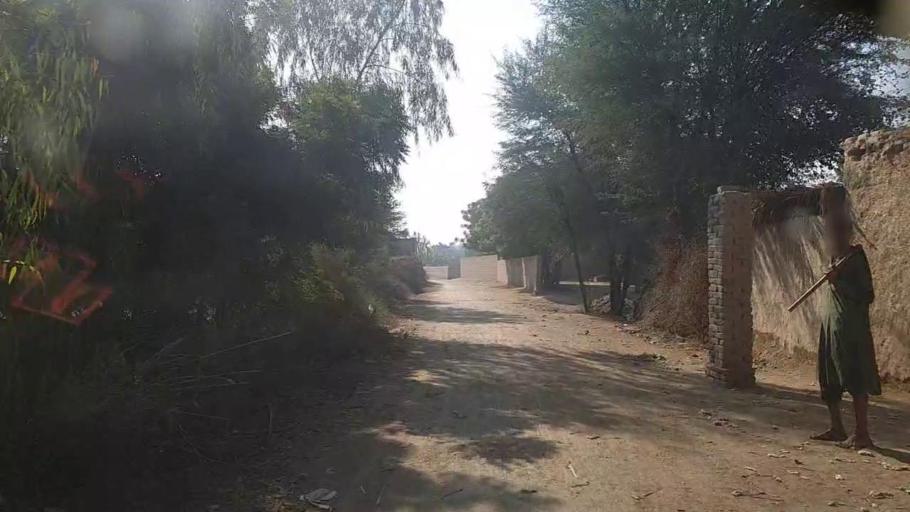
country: PK
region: Sindh
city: Kandiari
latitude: 27.0226
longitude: 68.5078
